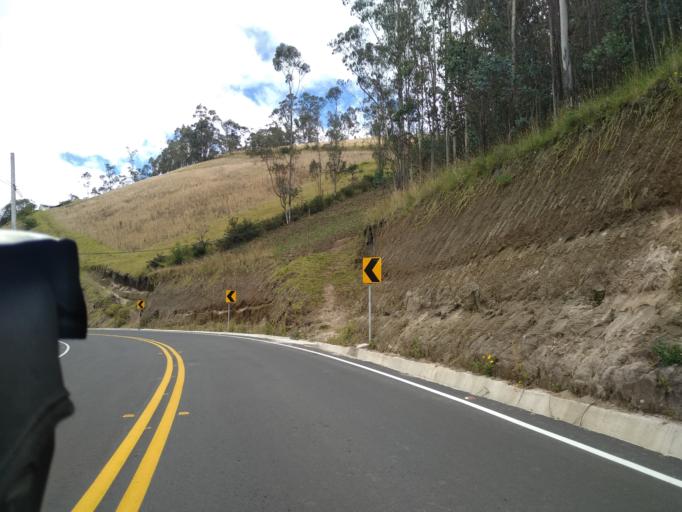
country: EC
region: Cotopaxi
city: Saquisili
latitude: -0.7110
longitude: -78.8827
